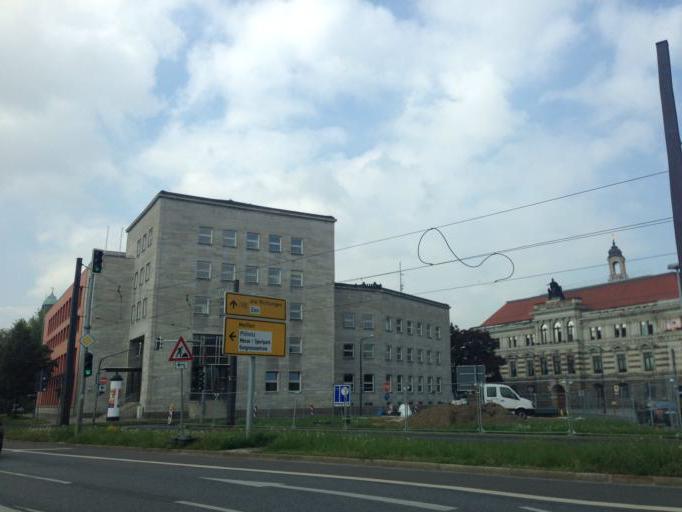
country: DE
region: Saxony
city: Dresden
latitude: 51.0517
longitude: 13.7470
